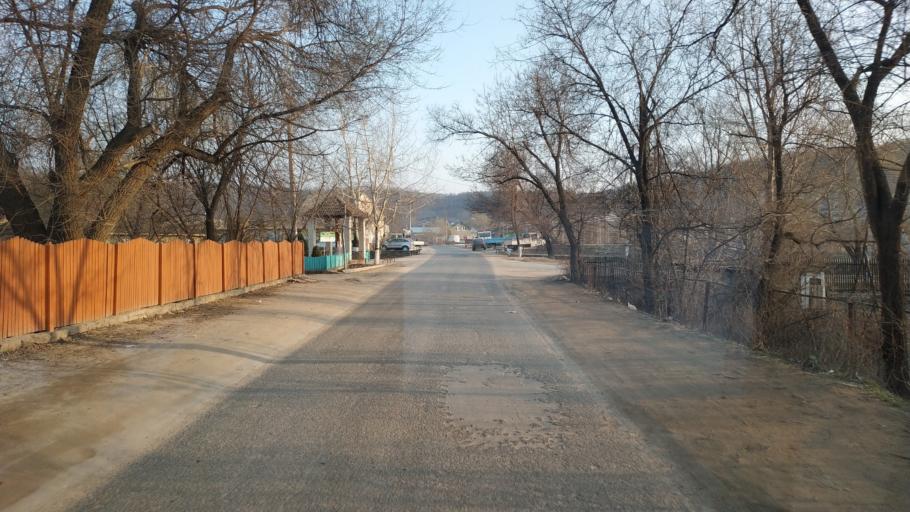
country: MD
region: Hincesti
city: Dancu
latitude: 46.7601
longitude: 28.3518
